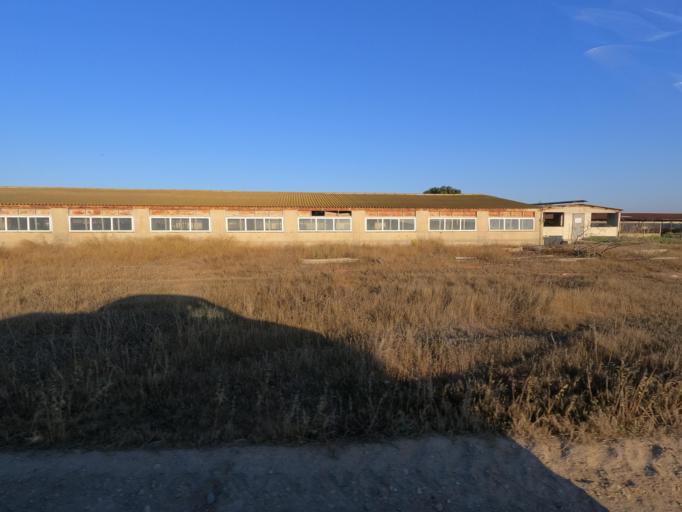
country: CY
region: Ammochostos
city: Avgorou
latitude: 35.0127
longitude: 33.8031
